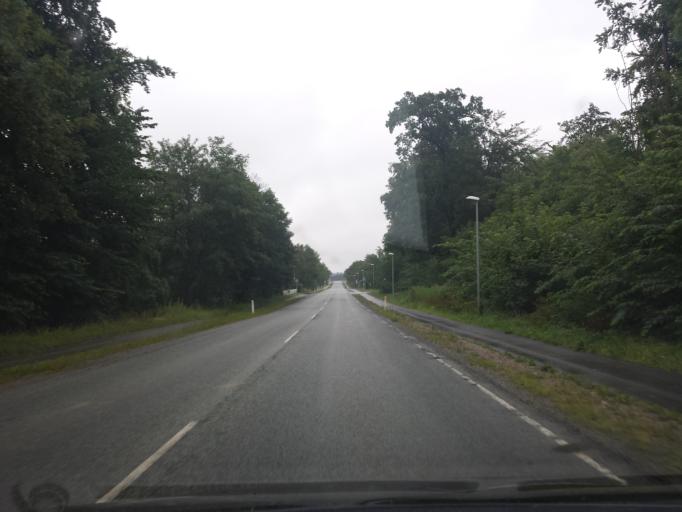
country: DK
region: South Denmark
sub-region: Sonderborg Kommune
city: Grasten
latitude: 54.9291
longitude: 9.6035
